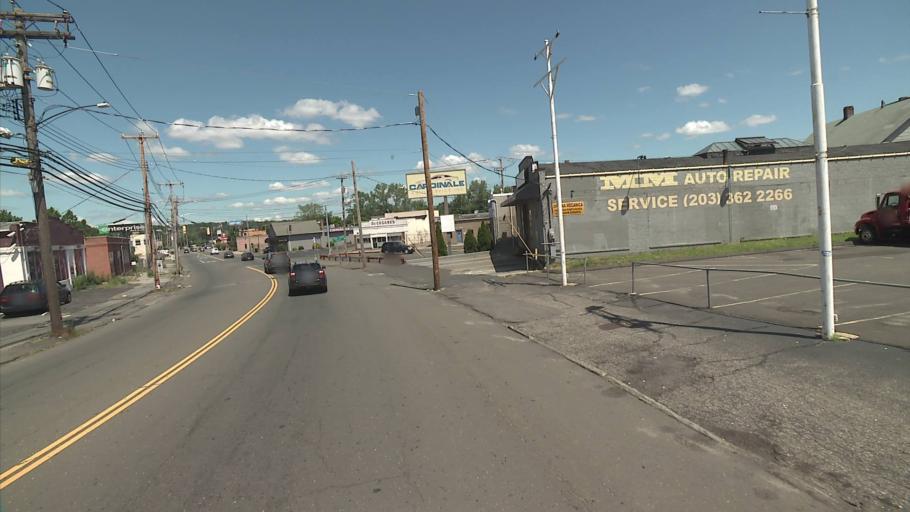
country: US
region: Connecticut
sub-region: Fairfield County
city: Bridgeport
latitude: 41.1977
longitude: -73.1925
